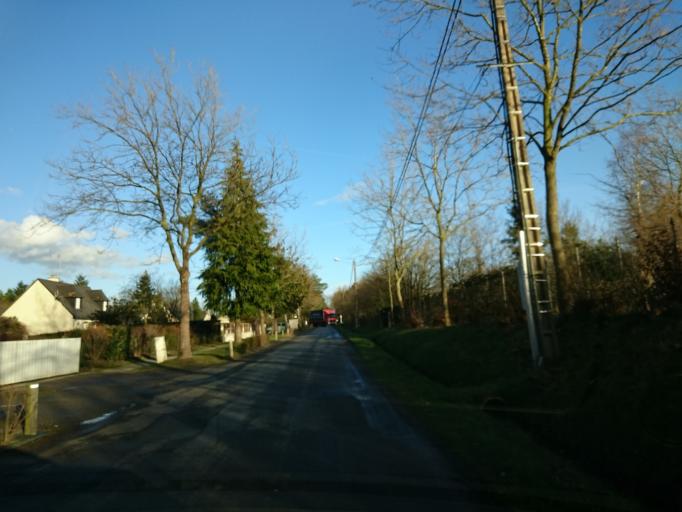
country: FR
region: Brittany
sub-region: Departement d'Ille-et-Vilaine
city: Crevin
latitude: 47.9431
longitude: -1.6553
